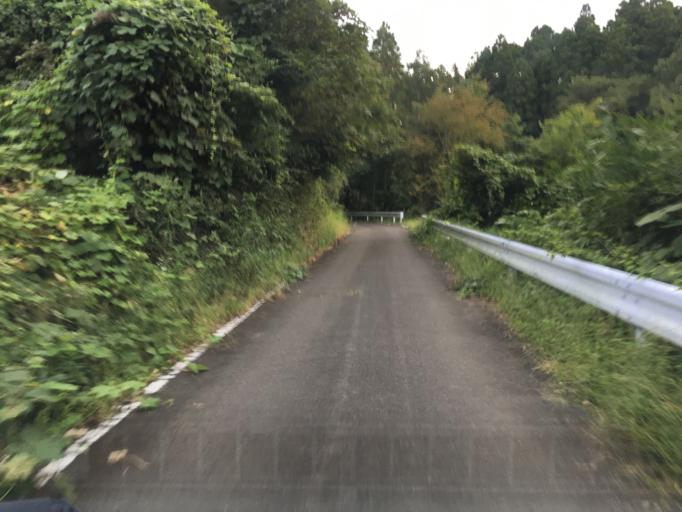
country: JP
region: Fukushima
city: Fukushima-shi
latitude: 37.7626
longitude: 140.5009
